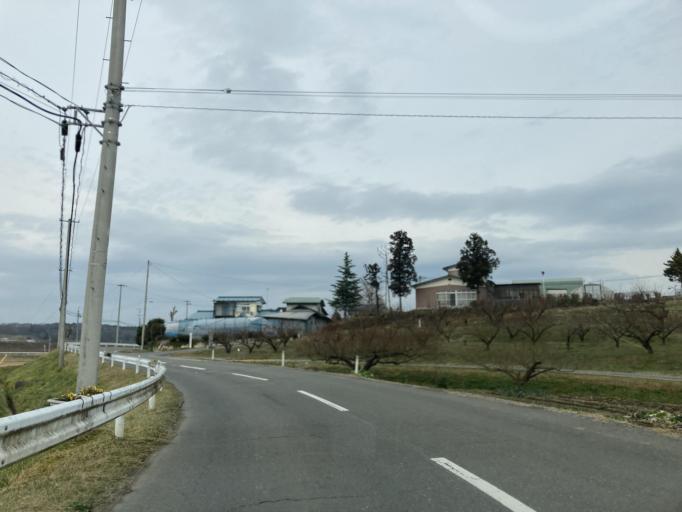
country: JP
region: Miyagi
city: Wakuya
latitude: 38.6872
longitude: 141.2768
